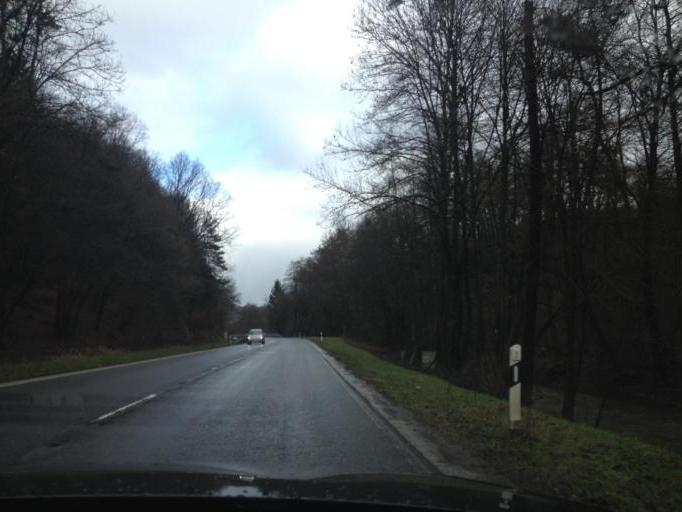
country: DE
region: Rheinland-Pfalz
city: Ellweiler
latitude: 49.6208
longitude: 7.1588
